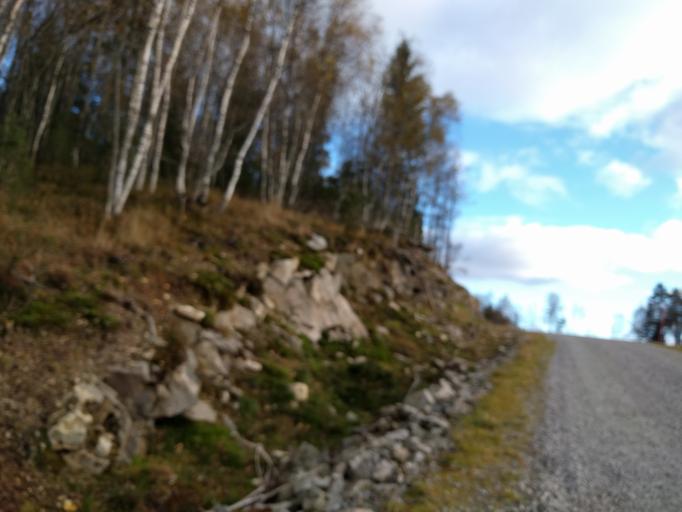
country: NO
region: Aust-Agder
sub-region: Evje og Hornnes
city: Evje
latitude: 58.6541
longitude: 7.9455
